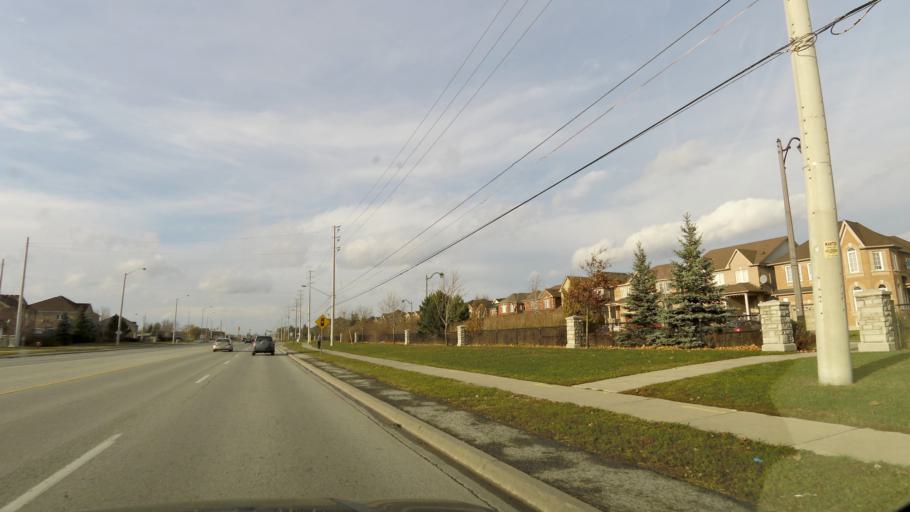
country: CA
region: Ontario
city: Brampton
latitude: 43.7784
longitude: -79.6715
